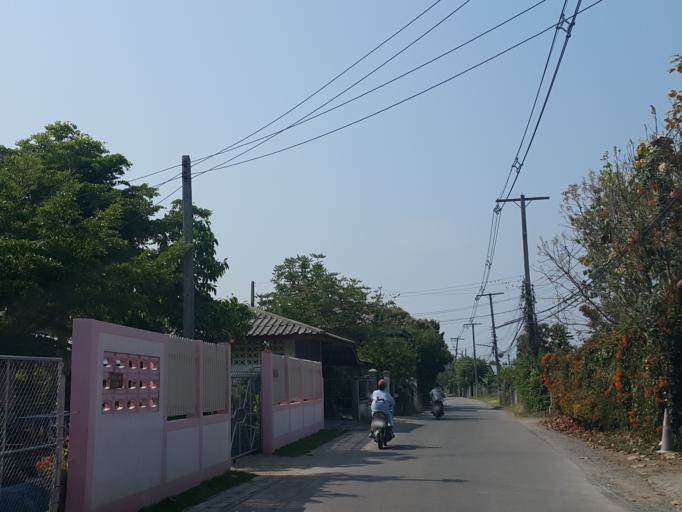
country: TH
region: Chiang Mai
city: San Kamphaeng
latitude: 18.7485
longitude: 99.1390
